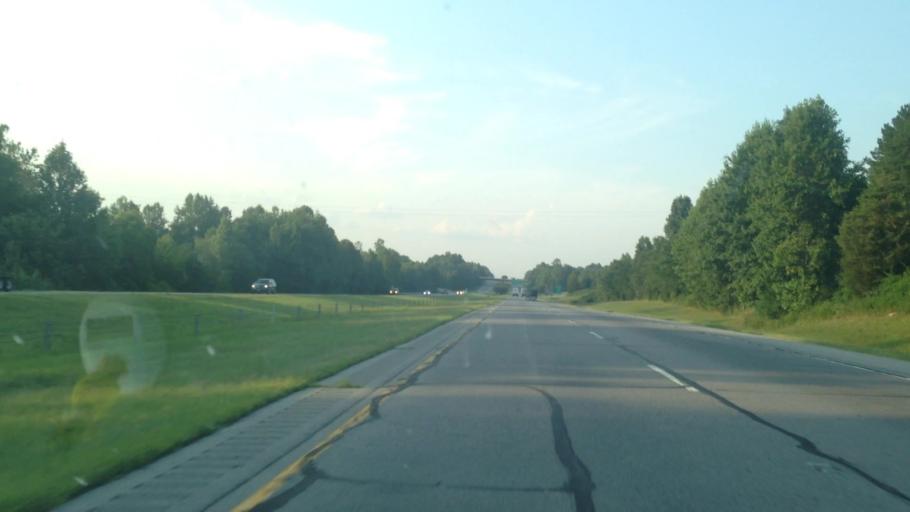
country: US
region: Virginia
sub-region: City of Danville
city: Danville
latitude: 36.5105
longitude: -79.4773
